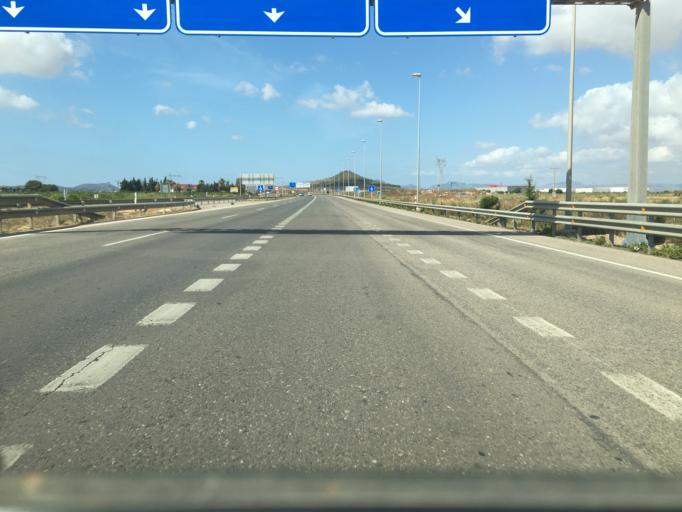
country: ES
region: Murcia
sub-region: Murcia
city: La Union
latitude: 37.6549
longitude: -0.9083
